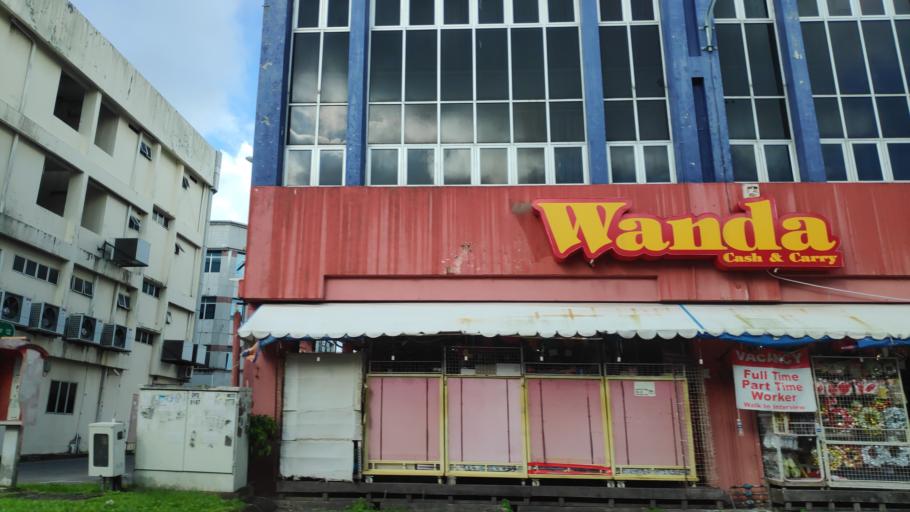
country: MY
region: Sarawak
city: Kuching
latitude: 1.5518
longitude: 110.3344
